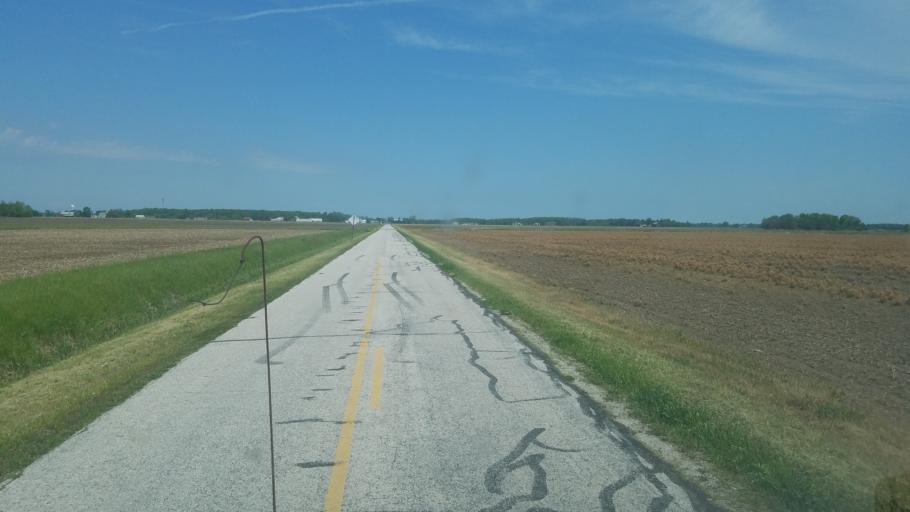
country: US
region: Ohio
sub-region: Ottawa County
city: Oak Harbor
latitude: 41.4589
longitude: -83.2016
